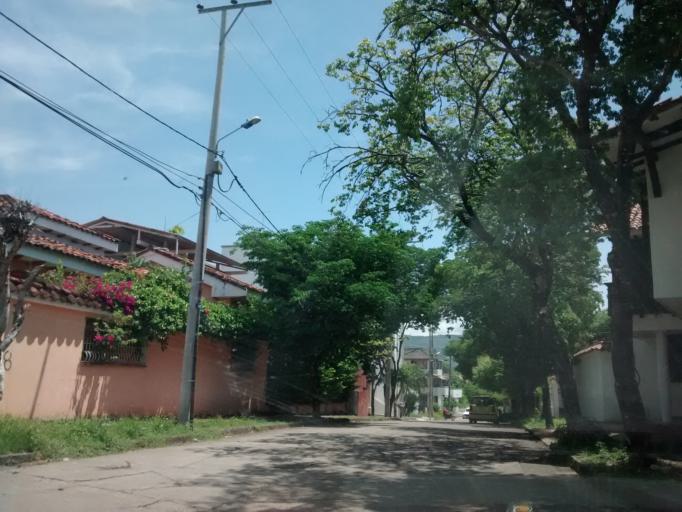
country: CO
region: Cundinamarca
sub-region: Girardot
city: Girardot City
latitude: 4.3063
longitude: -74.7999
